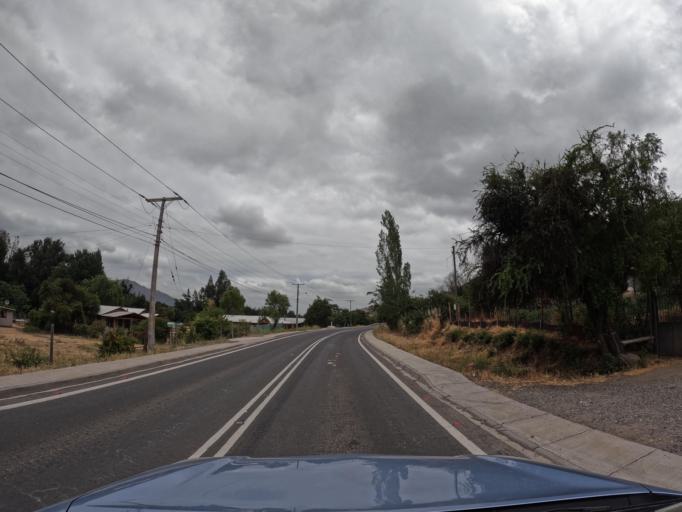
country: CL
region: Maule
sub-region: Provincia de Curico
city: Teno
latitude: -34.8113
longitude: -71.2145
